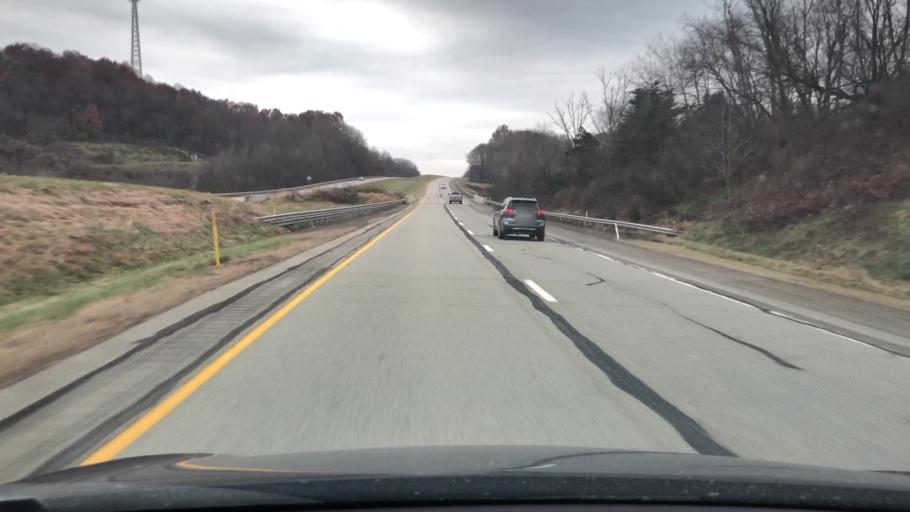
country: US
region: Pennsylvania
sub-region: Armstrong County
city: Ford City
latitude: 40.7817
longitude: -79.5865
